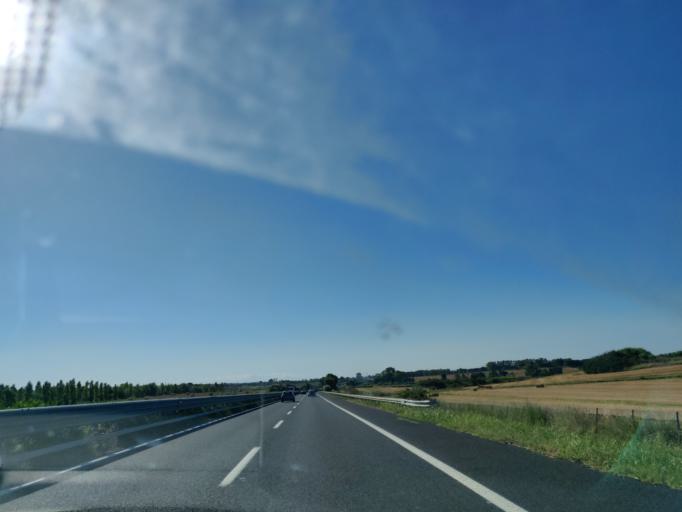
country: IT
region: Latium
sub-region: Citta metropolitana di Roma Capitale
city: Marina di Cerveteri
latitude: 42.0012
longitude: 12.0420
